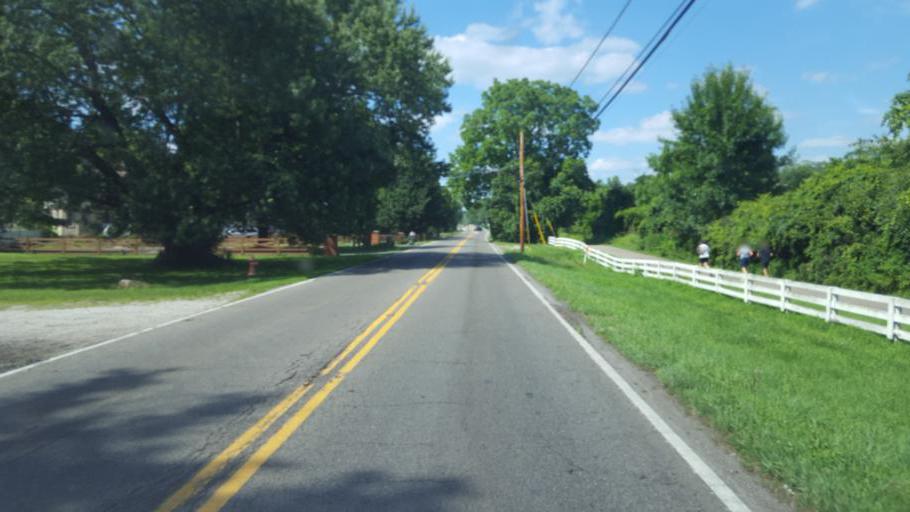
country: US
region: Ohio
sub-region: Franklin County
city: Bexley
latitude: 40.0108
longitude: -82.9346
